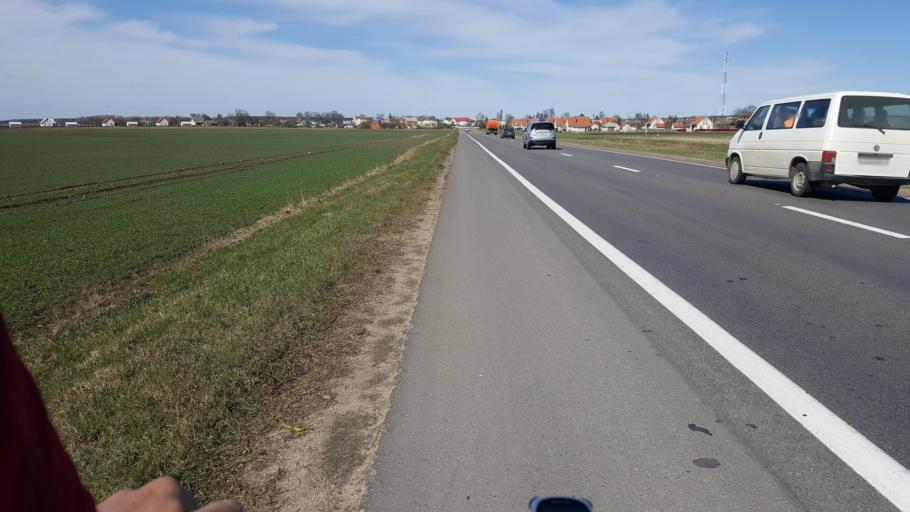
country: BY
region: Brest
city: Kamyanyets
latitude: 52.3188
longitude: 23.7818
